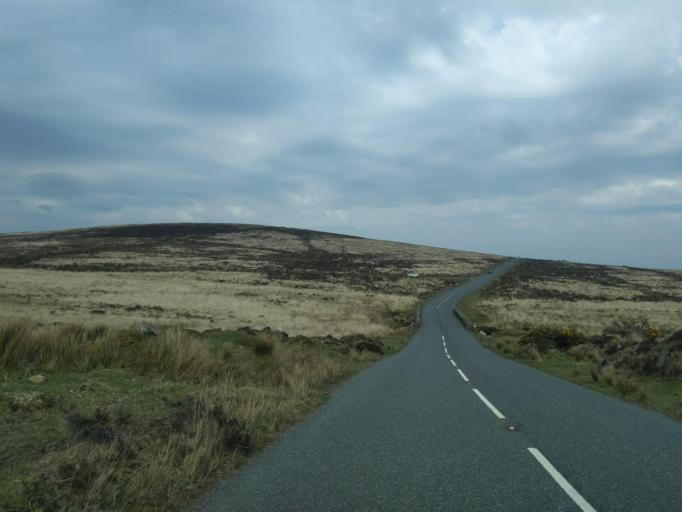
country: GB
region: England
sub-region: Devon
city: Ashburton
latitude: 50.6087
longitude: -3.8858
